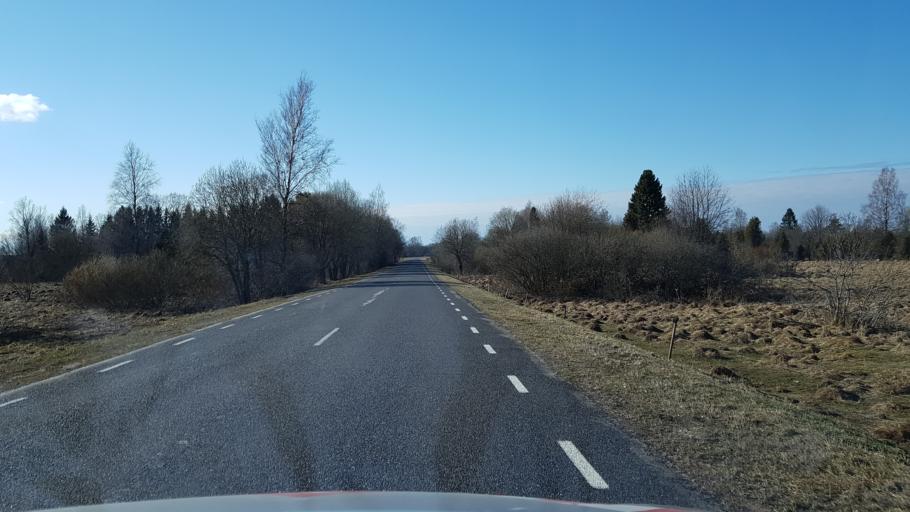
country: EE
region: Laeaene-Virumaa
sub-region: Kadrina vald
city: Kadrina
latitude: 59.5308
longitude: 26.0620
